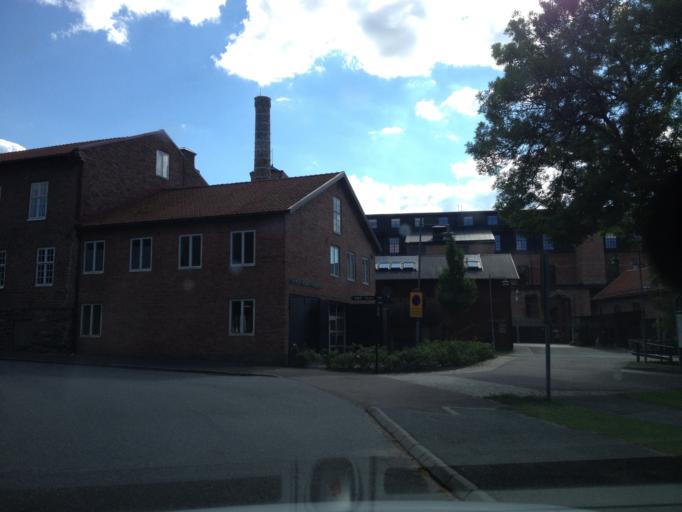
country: SE
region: Vaestra Goetaland
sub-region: Alingsas Kommun
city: Ingared
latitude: 57.8199
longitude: 12.4186
